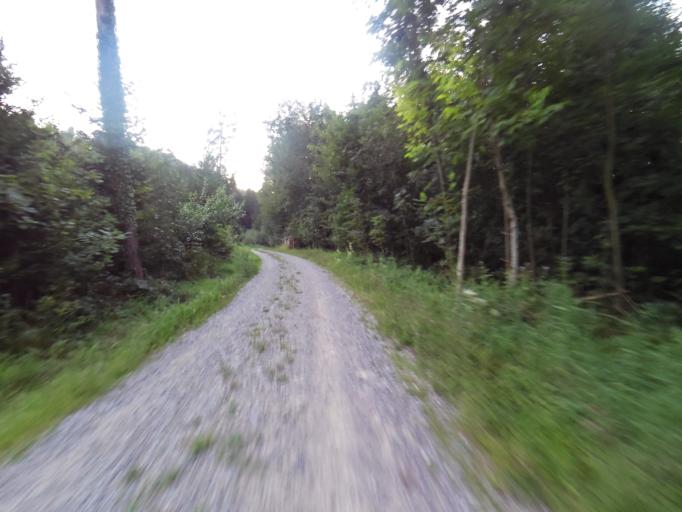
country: CH
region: Thurgau
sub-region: Weinfelden District
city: Wigoltingen
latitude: 47.5724
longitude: 9.0438
